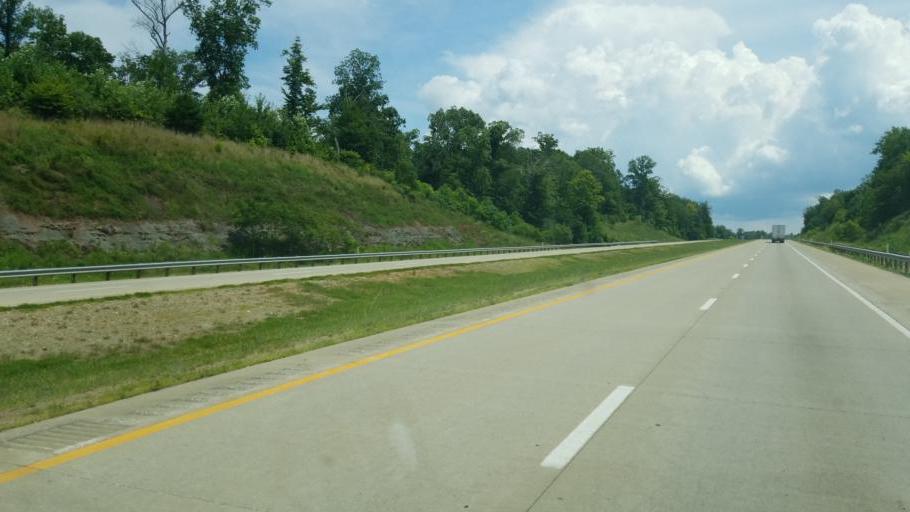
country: US
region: West Virginia
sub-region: Putnam County
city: Eleanor
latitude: 38.5436
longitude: -81.9702
